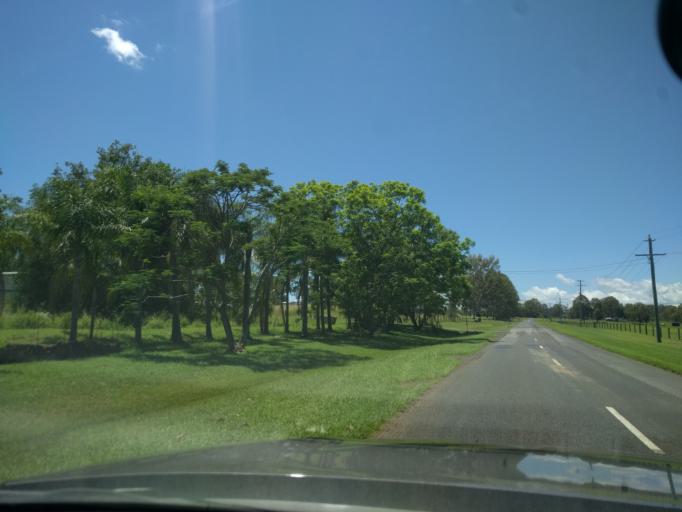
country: AU
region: Queensland
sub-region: Logan
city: Cedar Vale
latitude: -28.0015
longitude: 153.0048
